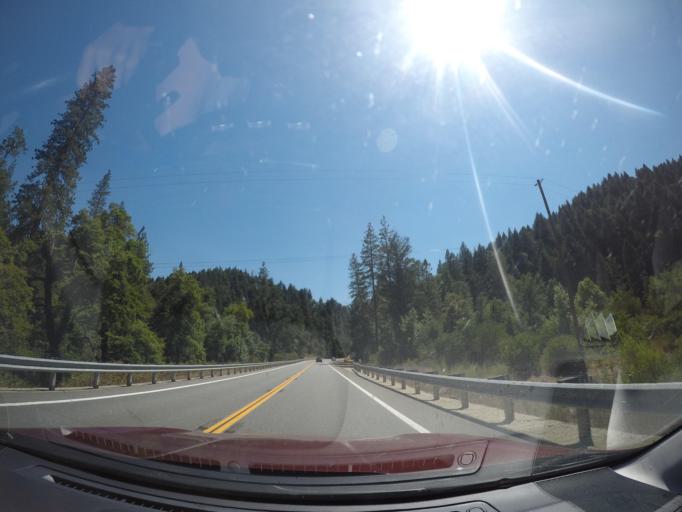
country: US
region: California
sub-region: Shasta County
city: Bella Vista
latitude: 40.7627
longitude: -122.0120
